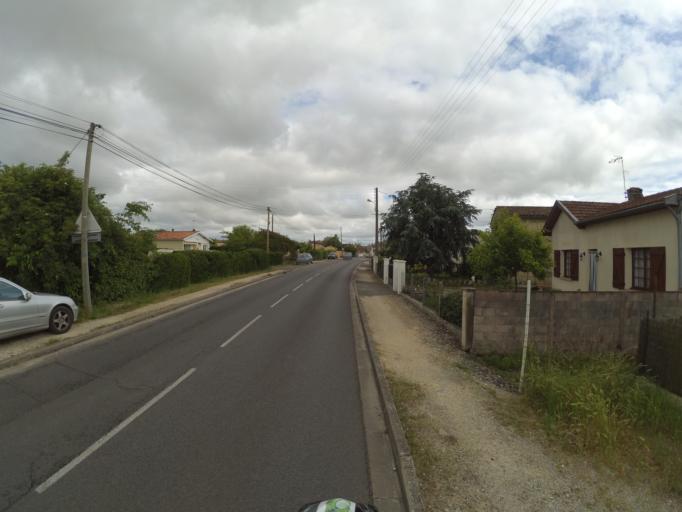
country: FR
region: Aquitaine
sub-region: Departement de la Gironde
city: Macau
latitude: 45.0098
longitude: -0.6165
